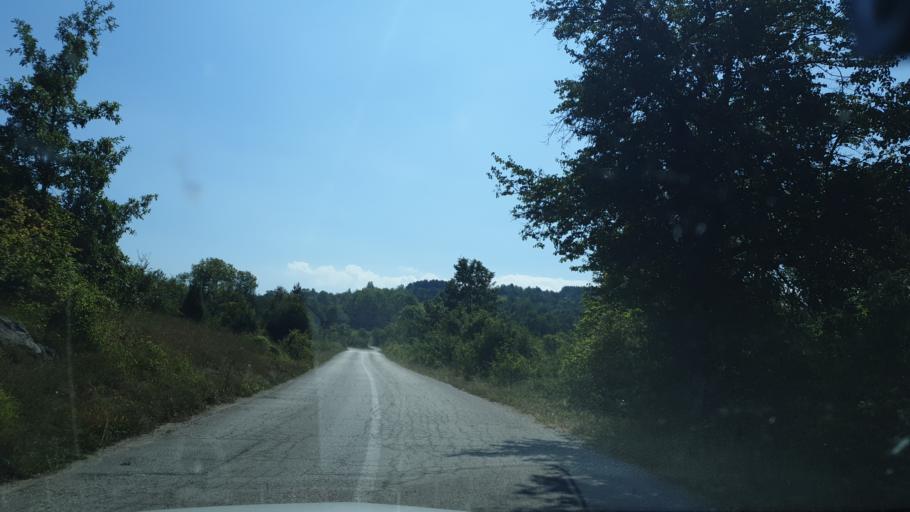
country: RS
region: Central Serbia
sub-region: Zlatiborski Okrug
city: Cajetina
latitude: 43.7003
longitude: 19.8538
